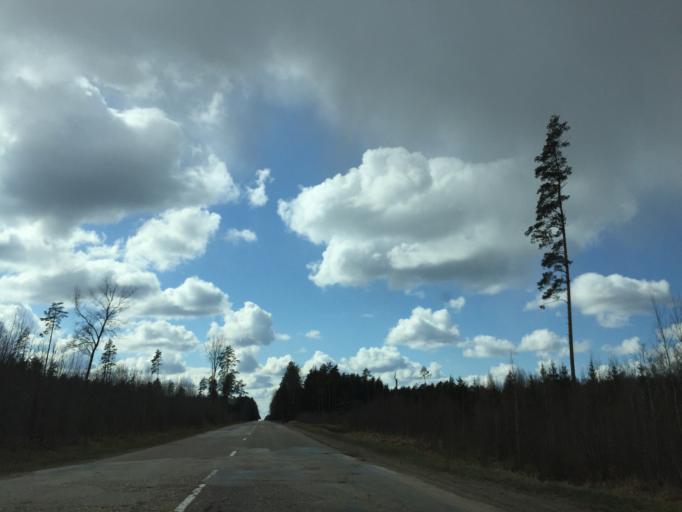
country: LV
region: Ropazu
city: Ropazi
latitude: 56.9537
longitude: 24.5501
